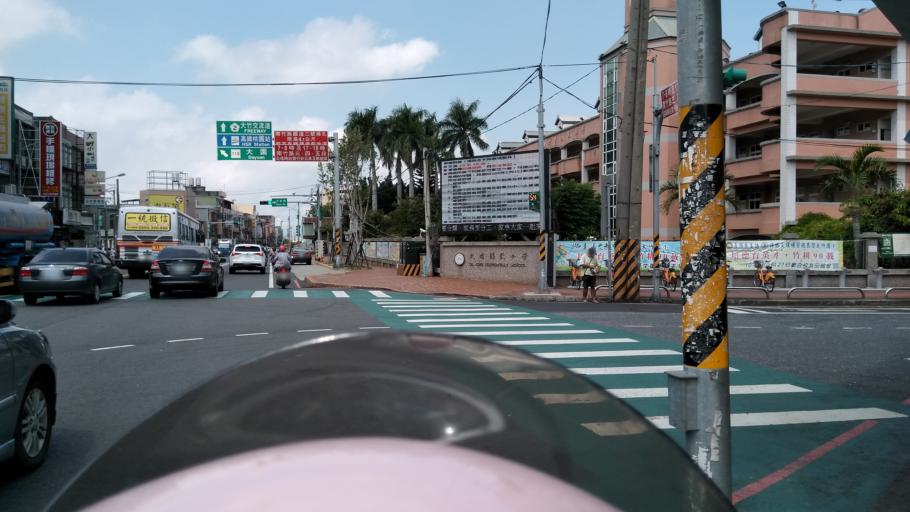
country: TW
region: Taiwan
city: Taoyuan City
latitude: 25.0245
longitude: 121.2588
